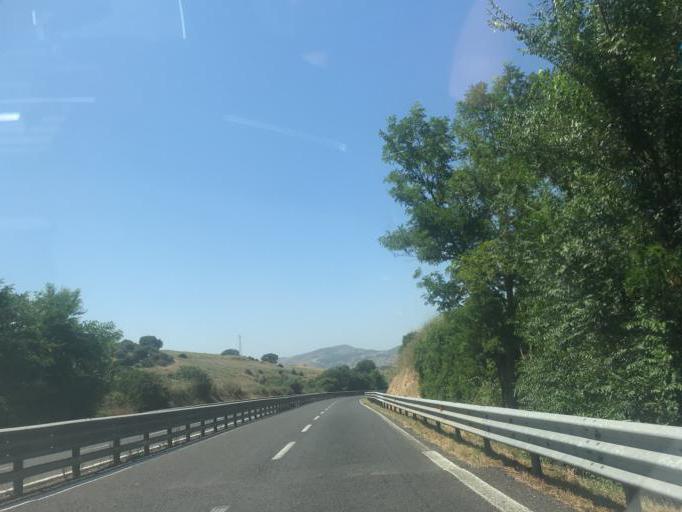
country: IT
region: Sardinia
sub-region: Provincia di Sassari
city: Codrongianos
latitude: 40.6627
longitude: 8.6695
